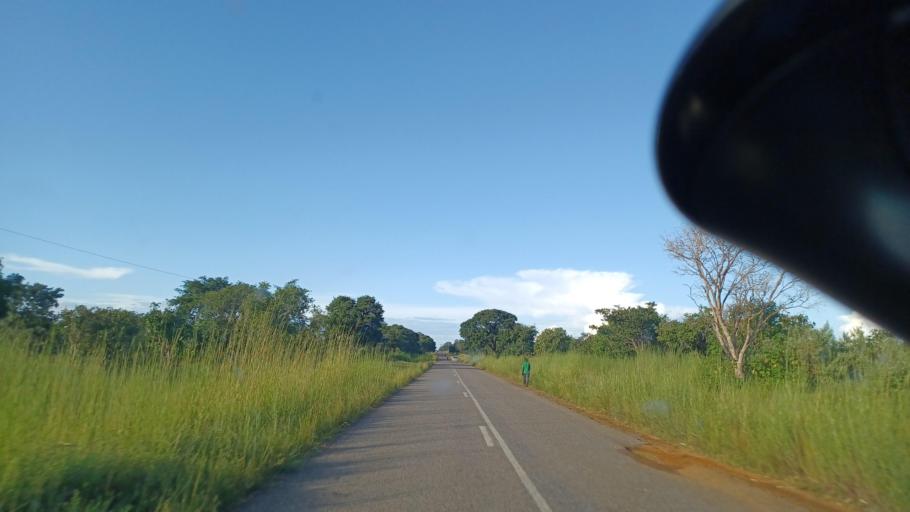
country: ZM
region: North-Western
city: Kalengwa
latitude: -13.2339
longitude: 24.7442
